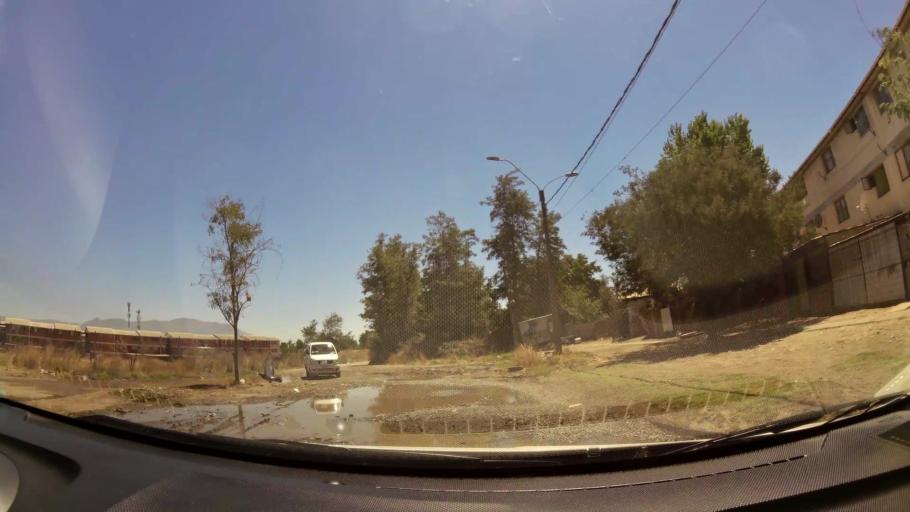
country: CL
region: O'Higgins
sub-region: Provincia de Cachapoal
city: Rancagua
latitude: -34.1522
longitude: -70.7167
